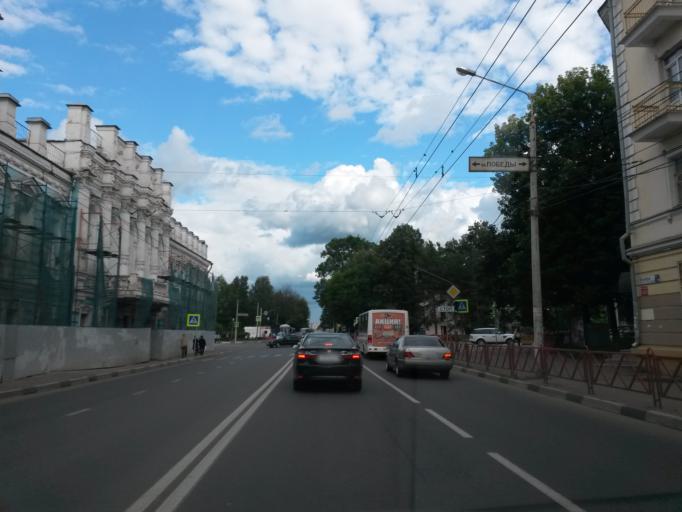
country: RU
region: Jaroslavl
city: Yaroslavl
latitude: 57.6349
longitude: 39.8710
